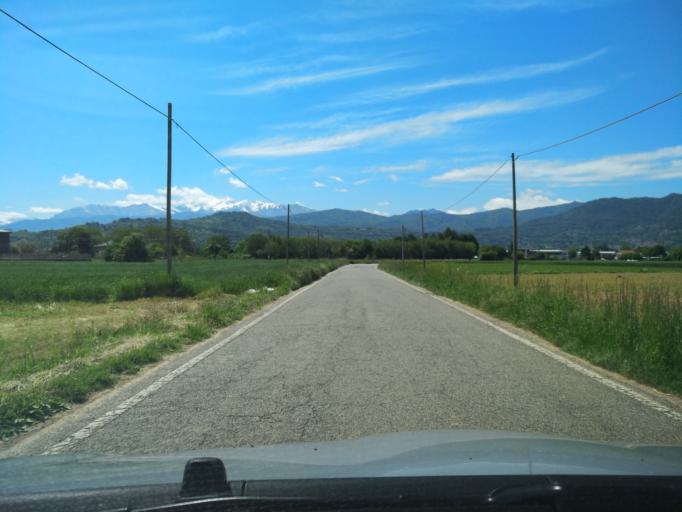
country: IT
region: Piedmont
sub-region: Provincia di Torino
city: Frossasco
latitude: 44.9102
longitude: 7.3706
